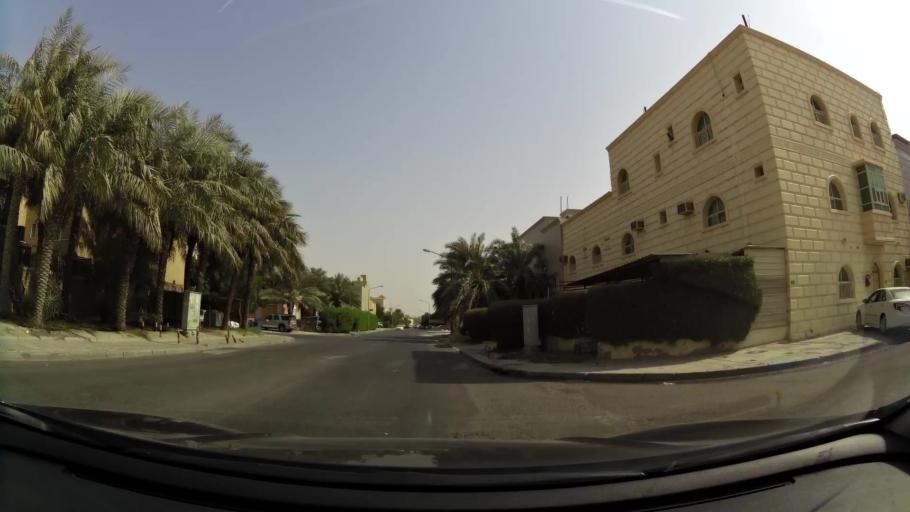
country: KW
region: Muhafazat al Jahra'
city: Al Jahra'
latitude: 29.3343
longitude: 47.6565
